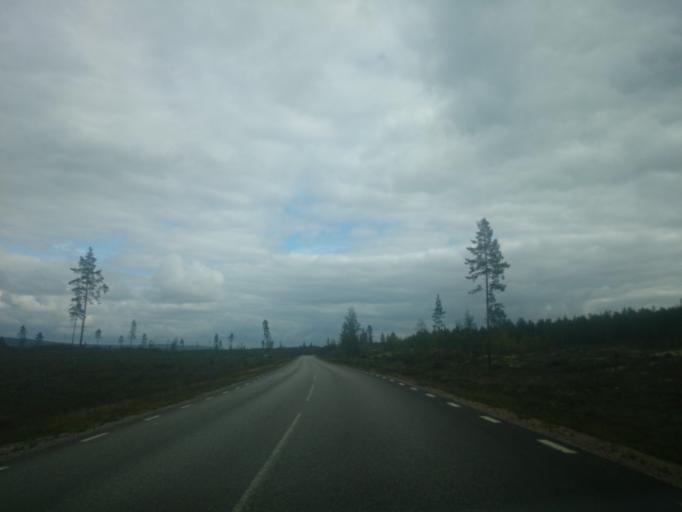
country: SE
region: Jaemtland
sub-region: Harjedalens Kommun
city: Sveg
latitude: 62.0295
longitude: 14.6847
